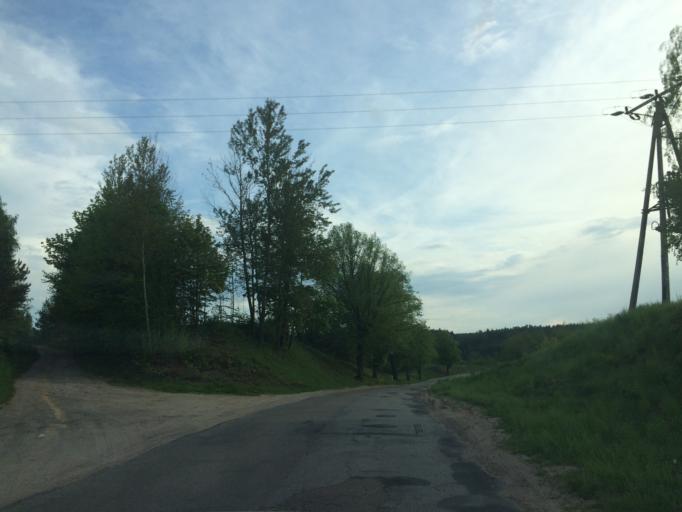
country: PL
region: Warmian-Masurian Voivodeship
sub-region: Powiat nowomiejski
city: Nowe Miasto Lubawskie
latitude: 53.4282
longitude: 19.6892
